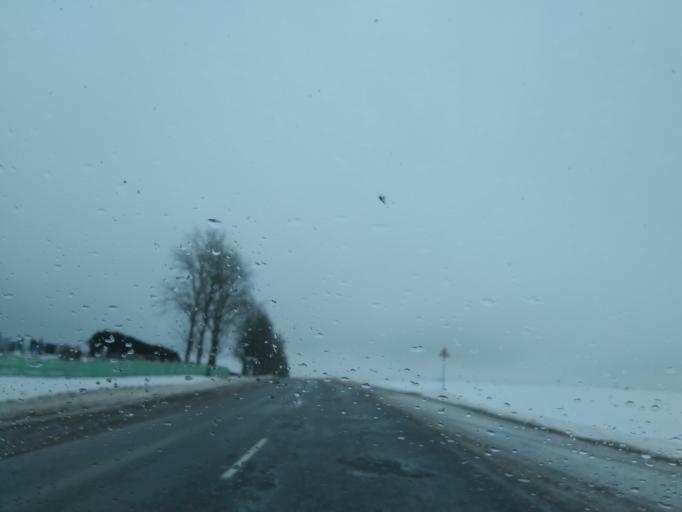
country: BY
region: Minsk
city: Stowbtsy
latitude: 53.5623
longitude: 26.7606
